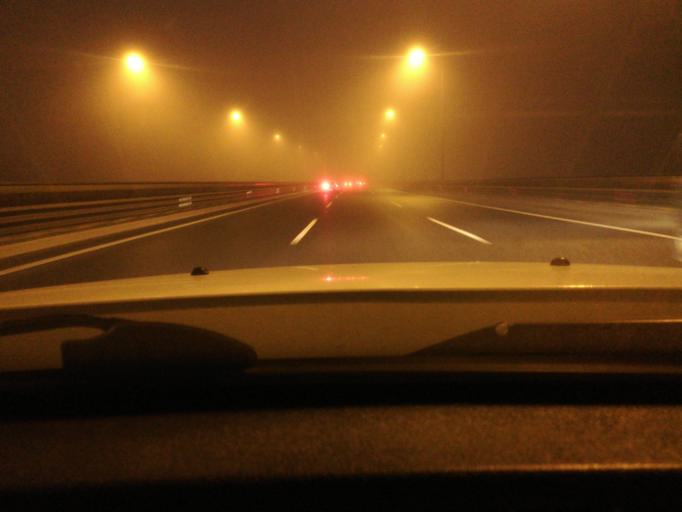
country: TR
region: Istanbul
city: Sultanbeyli
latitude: 40.9673
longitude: 29.3217
